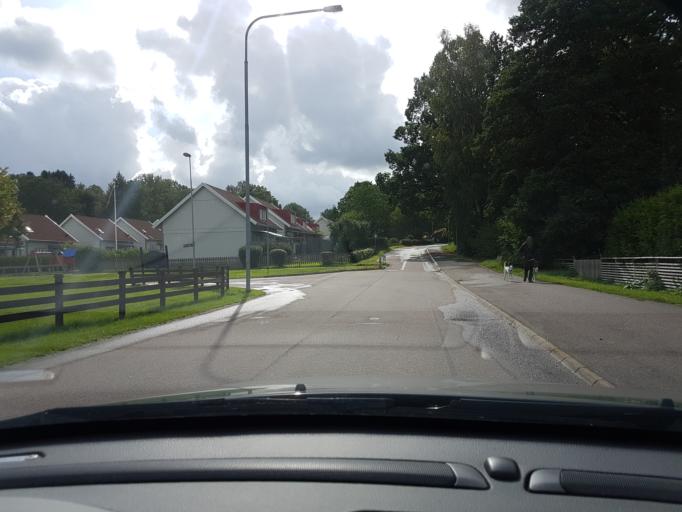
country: SE
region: Vaestra Goetaland
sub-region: Ale Kommun
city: Nodinge-Nol
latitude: 57.9060
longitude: 12.0548
